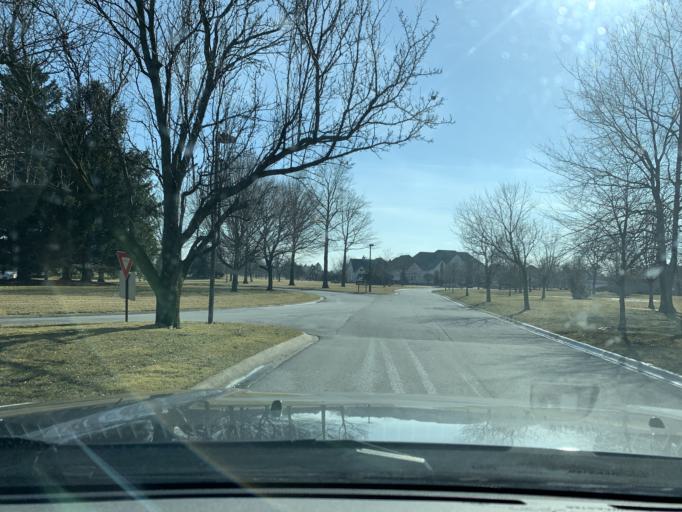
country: US
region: Indiana
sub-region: Lake County
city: Dyer
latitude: 41.5222
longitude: -87.4942
